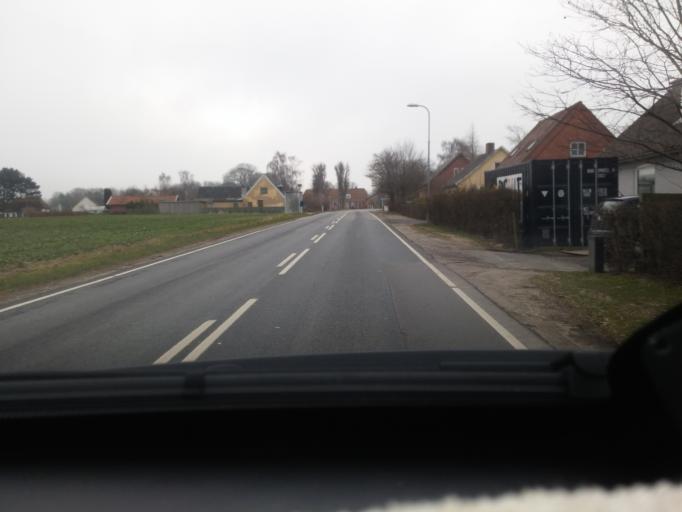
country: DK
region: South Denmark
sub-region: Nyborg Kommune
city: Ullerslev
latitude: 55.3698
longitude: 10.7272
